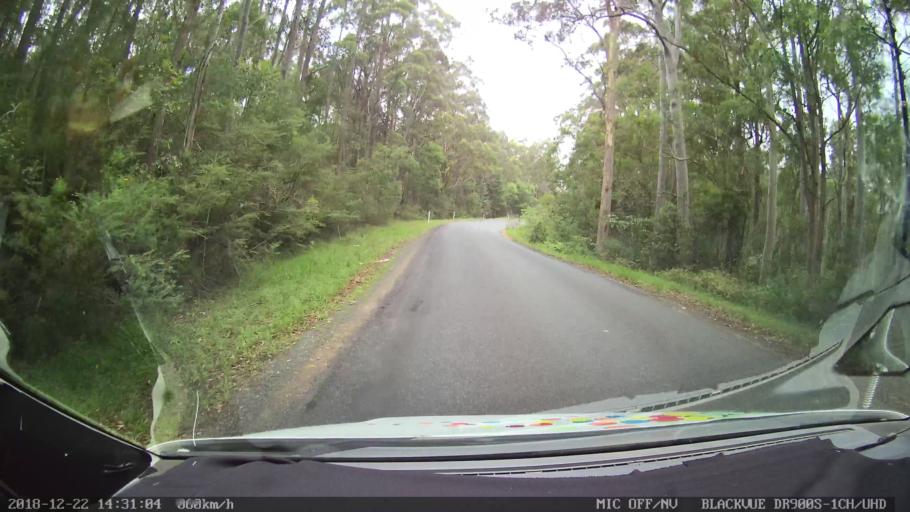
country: AU
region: New South Wales
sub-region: Bellingen
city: Dorrigo
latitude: -30.0927
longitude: 152.6323
